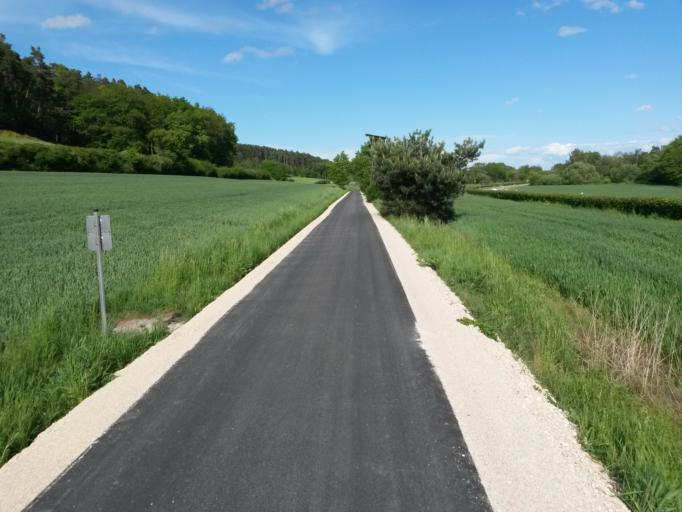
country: DE
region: Bavaria
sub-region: Regierungsbezirk Mittelfranken
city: Rosstal
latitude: 49.4263
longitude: 10.8886
